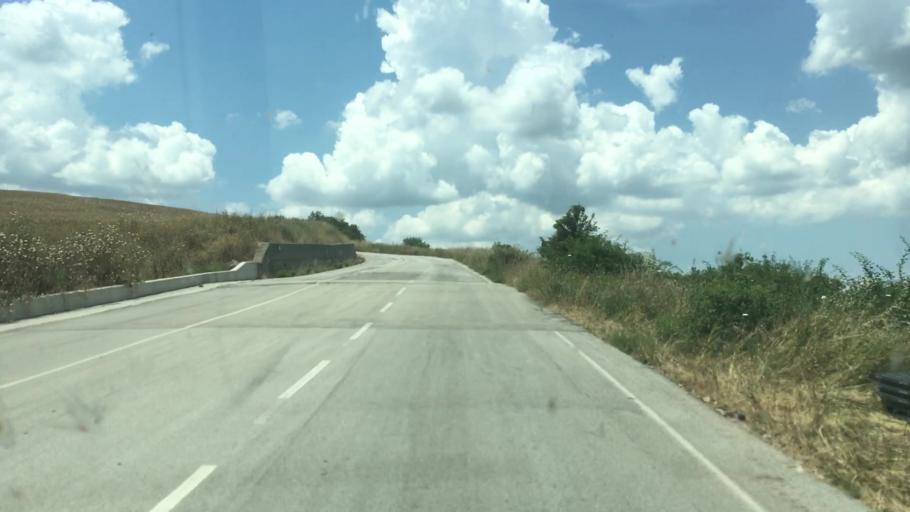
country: IT
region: Basilicate
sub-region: Provincia di Potenza
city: Tolve
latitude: 40.6848
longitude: 15.9781
